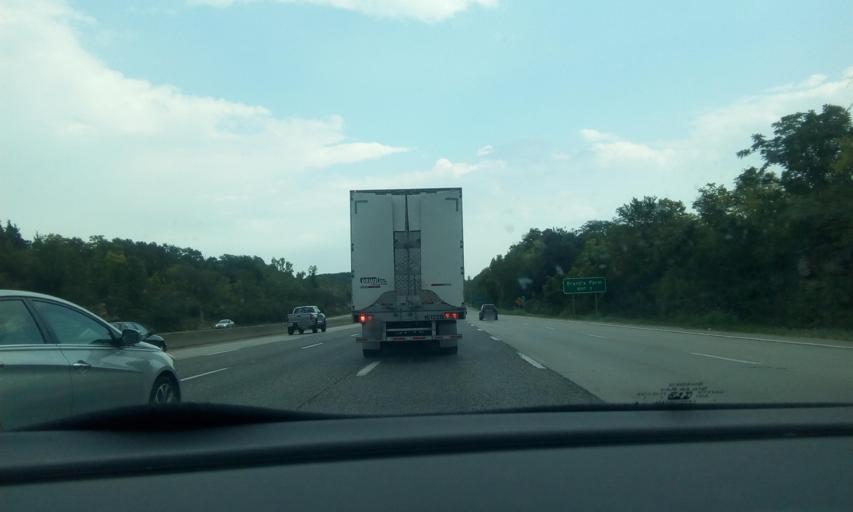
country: US
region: Missouri
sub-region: Saint Louis County
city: Sunset Hills
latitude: 38.5406
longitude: -90.4189
